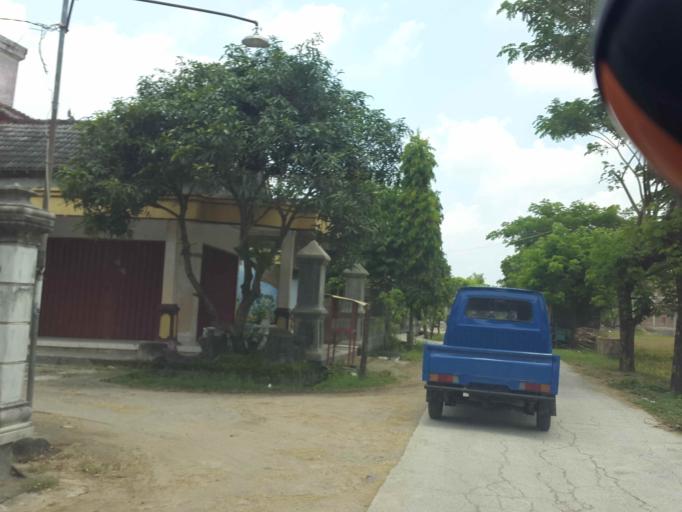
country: ID
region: Central Java
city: Sragen
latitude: -7.4041
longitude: 110.9991
